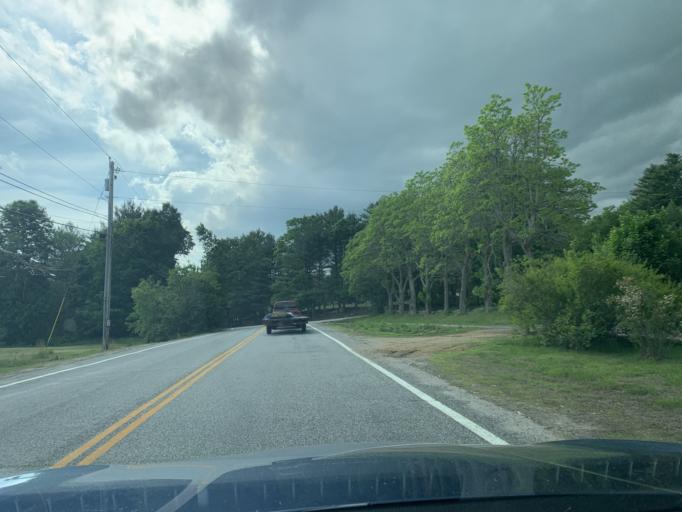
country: US
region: Rhode Island
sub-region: Kent County
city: Coventry
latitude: 41.7025
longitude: -71.7777
